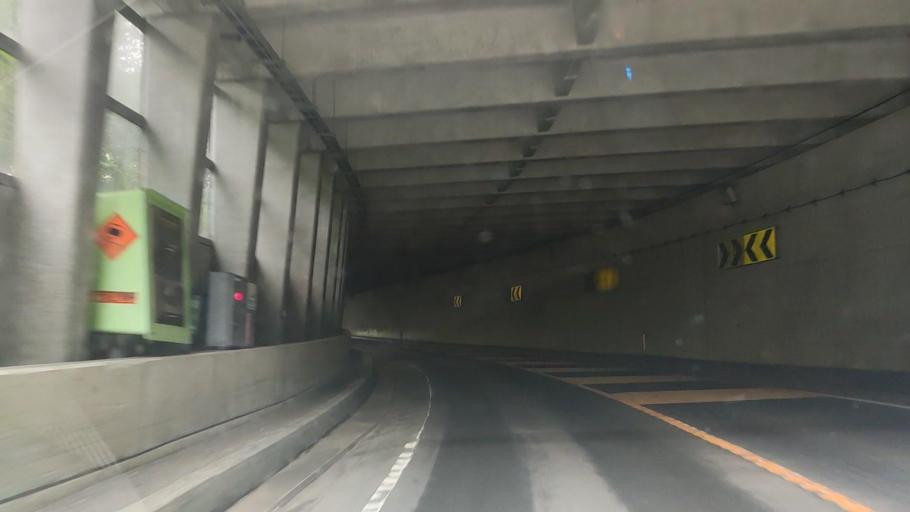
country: JP
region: Hokkaido
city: Otaru
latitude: 43.0878
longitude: 141.0558
